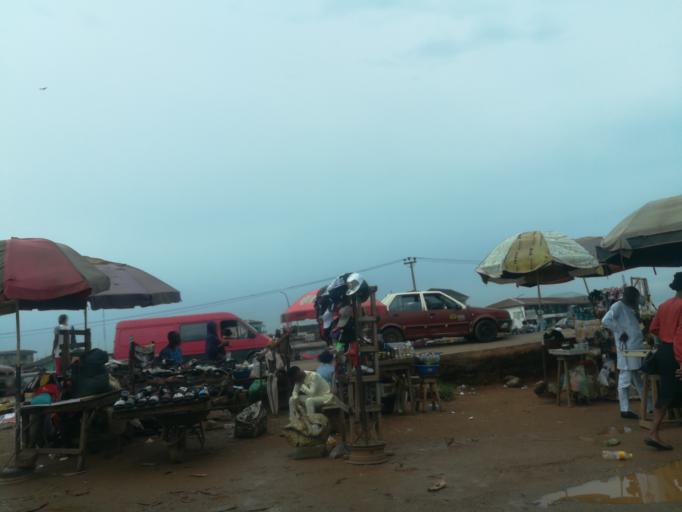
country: NG
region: Oyo
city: Ibadan
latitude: 7.4014
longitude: 3.9433
